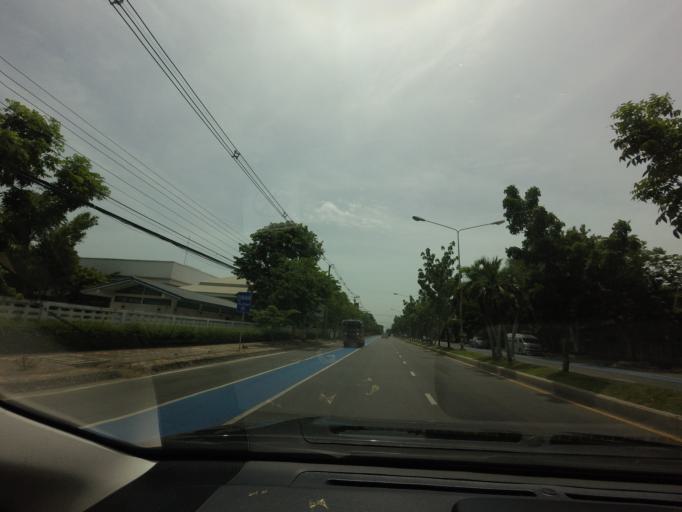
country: TH
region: Chon Buri
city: Chon Buri
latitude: 13.2941
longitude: 100.9102
